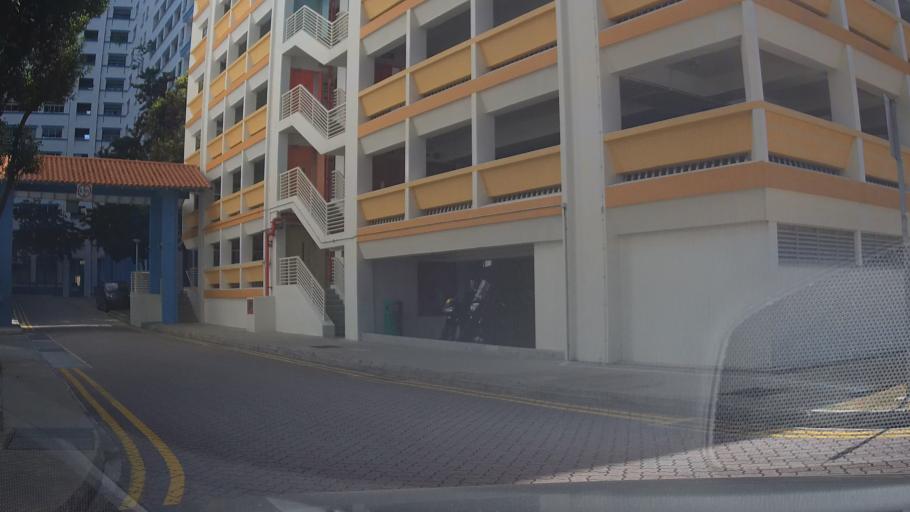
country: SG
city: Singapore
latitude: 1.3647
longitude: 103.9597
